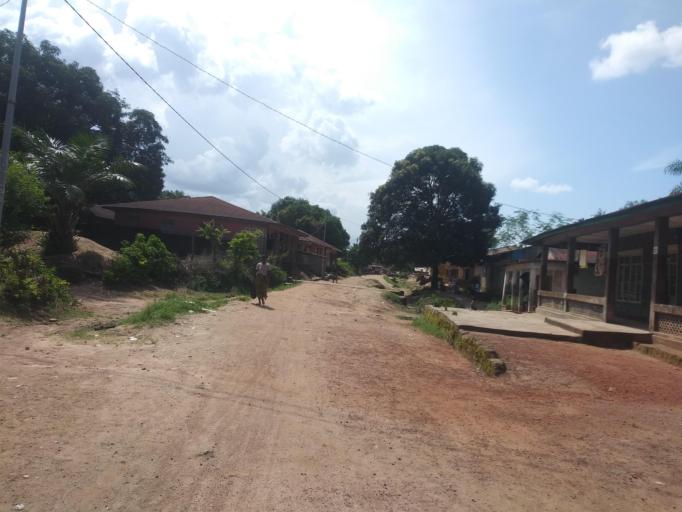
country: SL
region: Northern Province
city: Makeni
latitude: 8.8856
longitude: -12.0376
